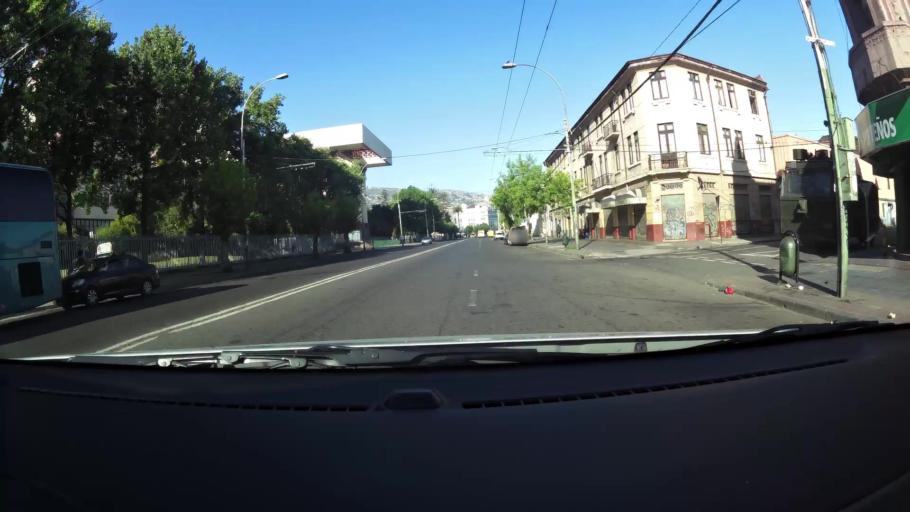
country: CL
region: Valparaiso
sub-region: Provincia de Valparaiso
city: Valparaiso
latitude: -33.0470
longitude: -71.6046
